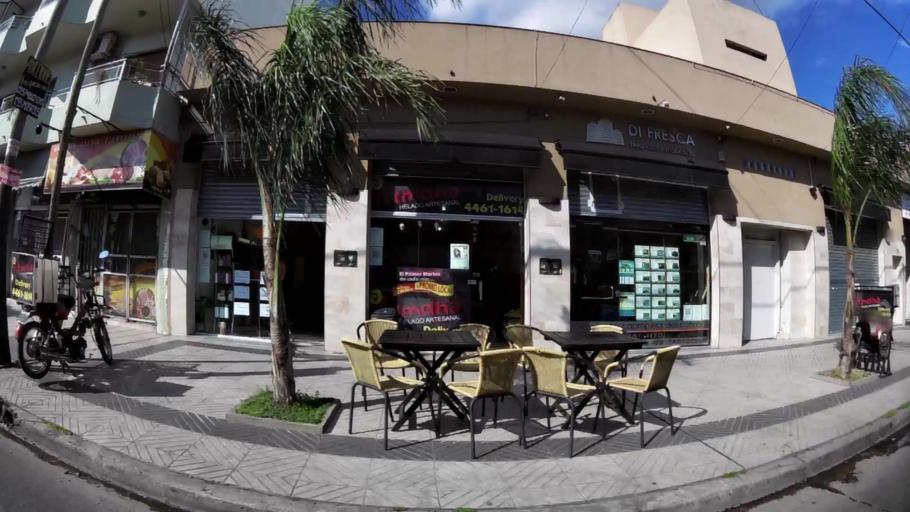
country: AR
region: Buenos Aires
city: San Justo
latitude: -34.6688
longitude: -58.5735
